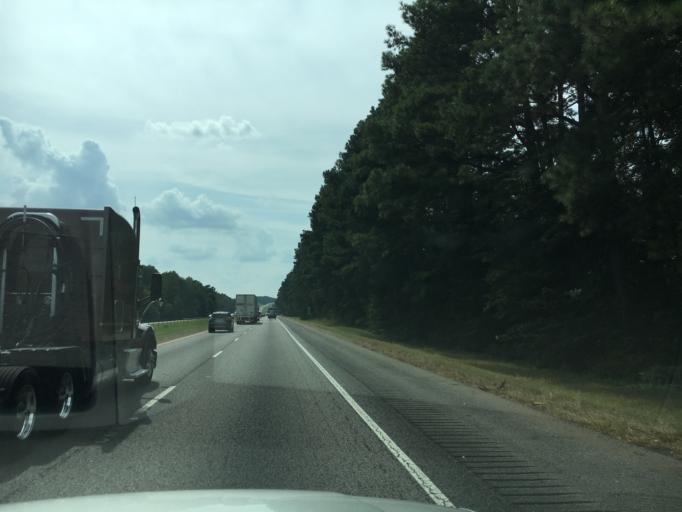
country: US
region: Georgia
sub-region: Jackson County
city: Braselton
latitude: 34.1322
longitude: -83.6856
